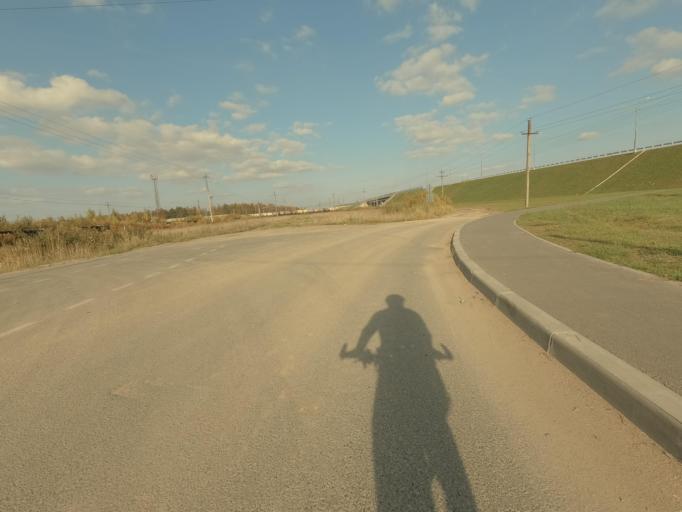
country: RU
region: Leningrad
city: Mga
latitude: 59.7519
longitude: 31.0891
